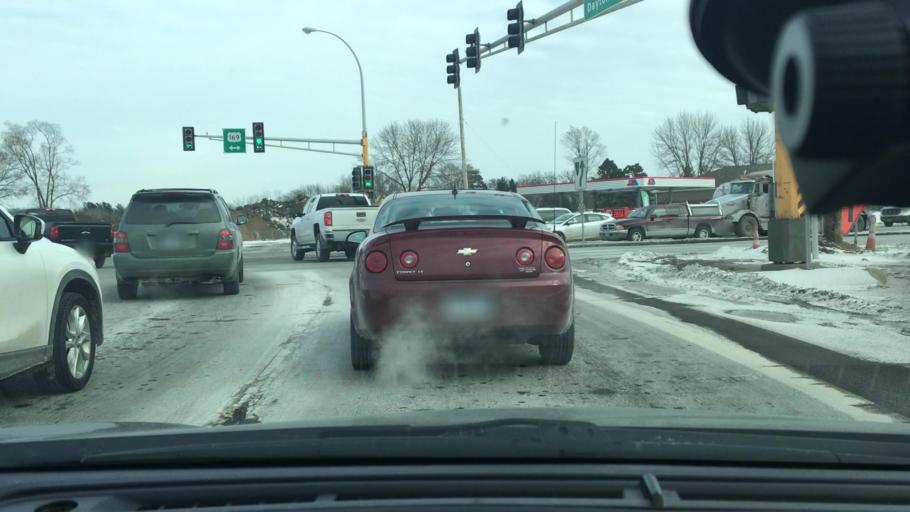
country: US
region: Minnesota
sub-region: Hennepin County
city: Champlin
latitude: 45.1891
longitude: -93.3971
